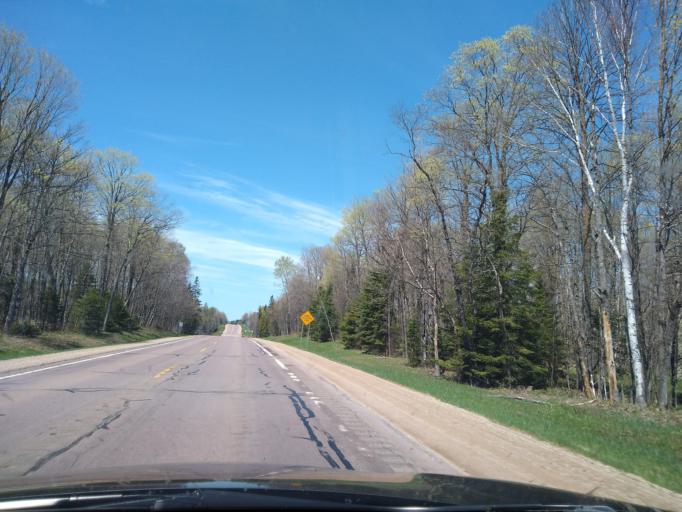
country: US
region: Michigan
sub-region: Marquette County
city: K. I. Sawyer Air Force Base
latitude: 46.2567
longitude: -87.0892
